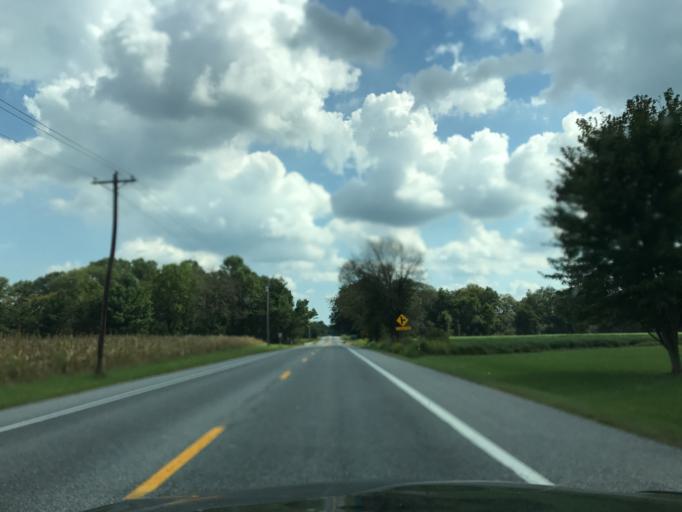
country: US
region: Delaware
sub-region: Kent County
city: Clayton
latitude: 39.1946
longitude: -75.7813
